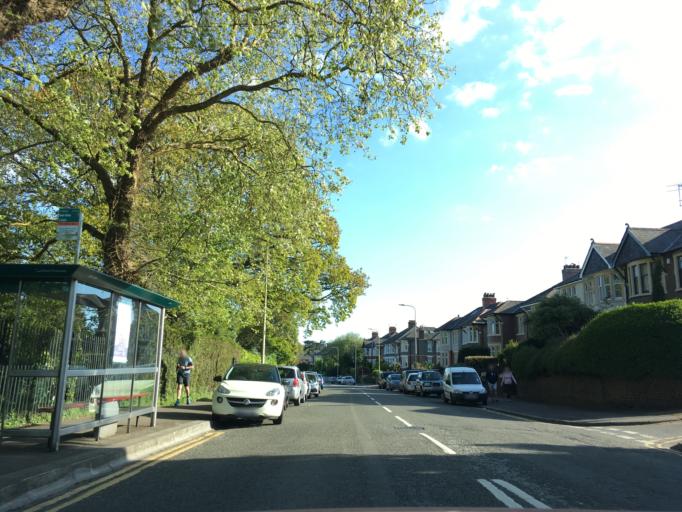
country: GB
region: Wales
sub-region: Cardiff
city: Cardiff
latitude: 51.5062
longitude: -3.1765
